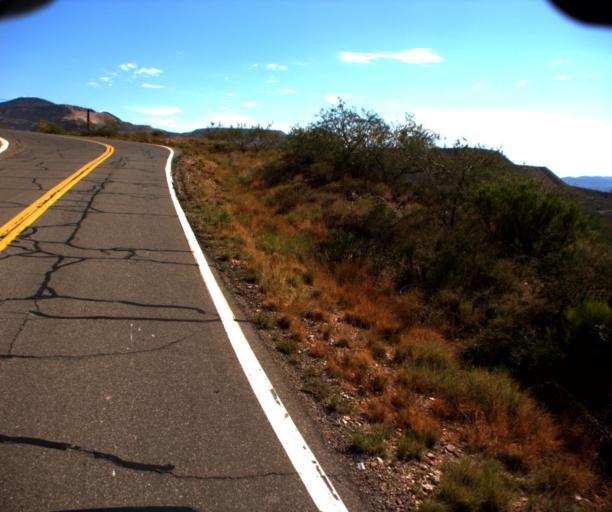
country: US
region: Arizona
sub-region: Greenlee County
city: Morenci
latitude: 33.0725
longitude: -109.3642
